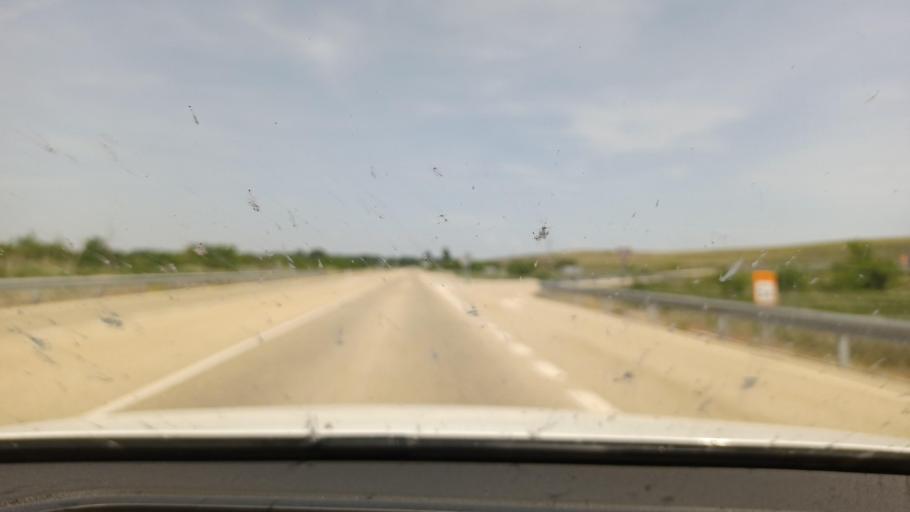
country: ES
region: Castille and Leon
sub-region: Provincia de Soria
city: Velamazan
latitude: 41.4740
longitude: -2.6909
